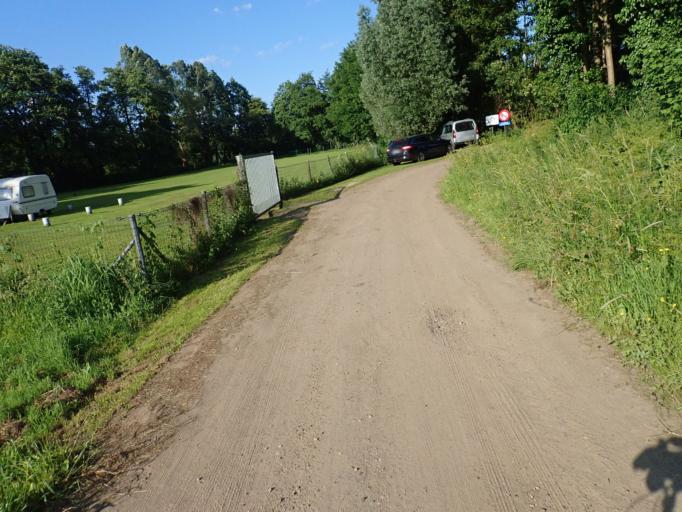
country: BE
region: Flanders
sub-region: Provincie Antwerpen
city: Zandhoven
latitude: 51.1866
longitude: 4.6574
